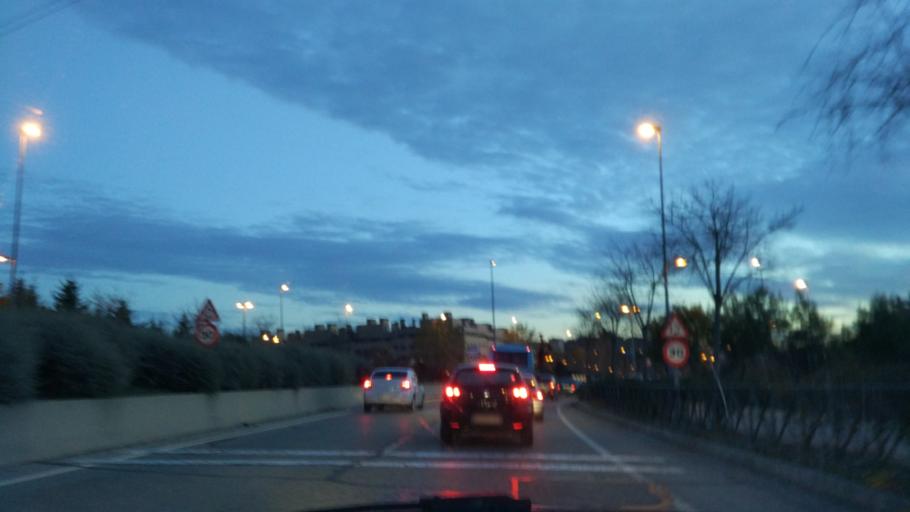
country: ES
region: Madrid
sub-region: Provincia de Madrid
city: Leganes
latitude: 40.3475
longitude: -3.7703
